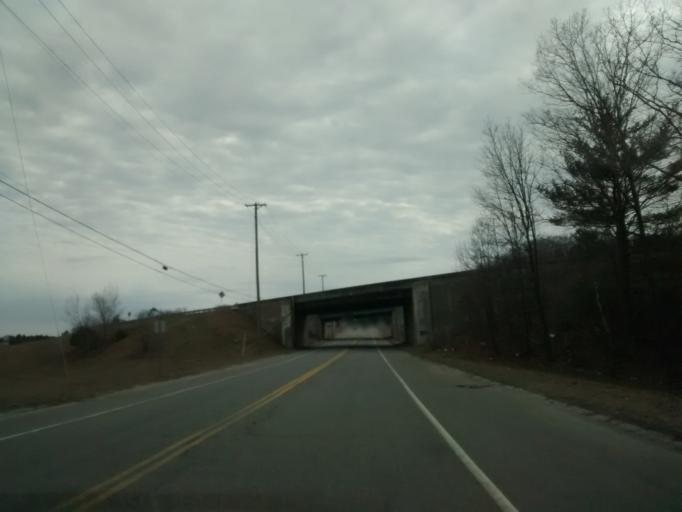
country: US
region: Massachusetts
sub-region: Worcester County
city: East Douglas
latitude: 42.0904
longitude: -71.6950
